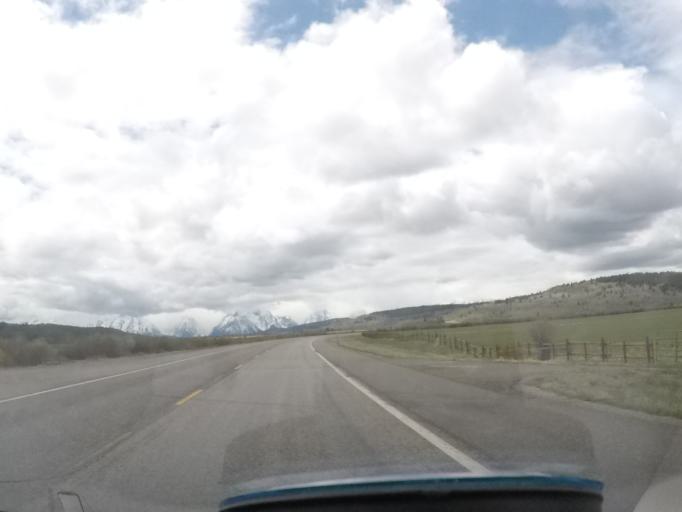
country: US
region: Wyoming
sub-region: Teton County
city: Jackson
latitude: 43.8318
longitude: -110.4173
